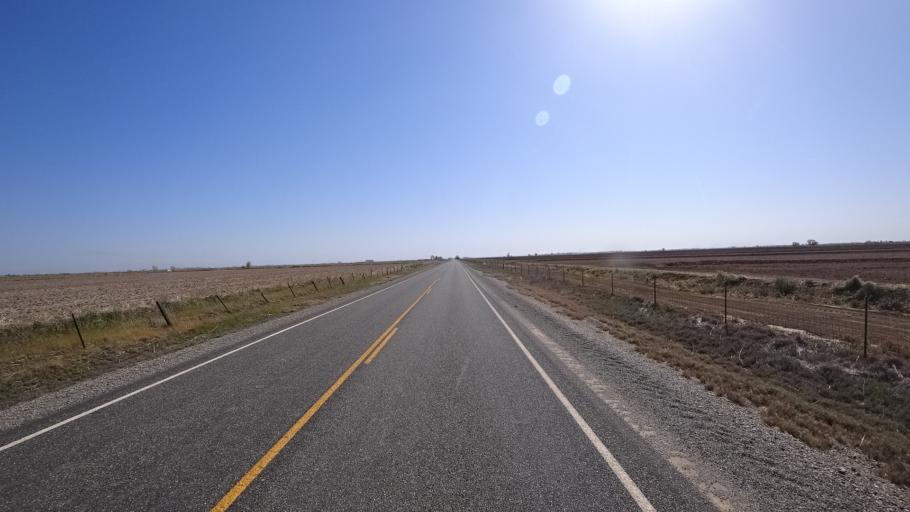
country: US
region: California
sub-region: Glenn County
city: Willows
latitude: 39.4656
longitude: -122.1890
